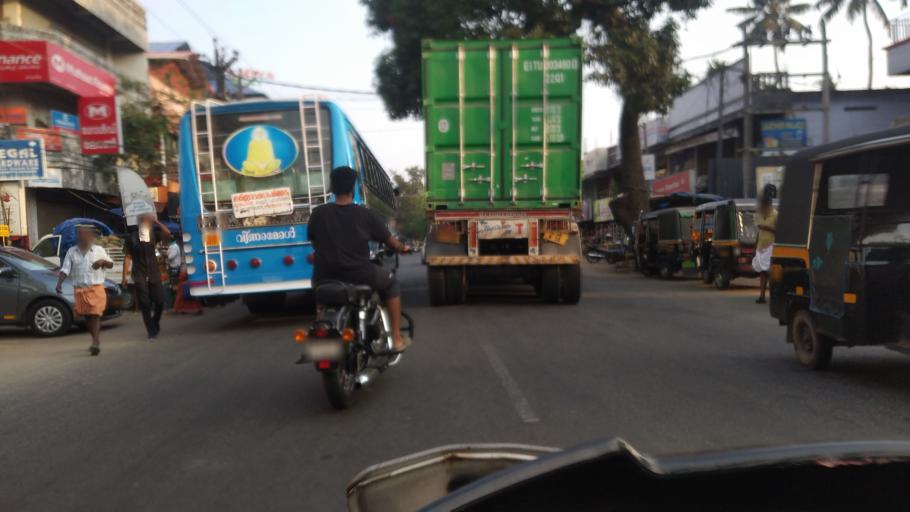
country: IN
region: Kerala
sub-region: Thrissur District
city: Irinjalakuda
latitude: 10.3198
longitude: 76.1455
